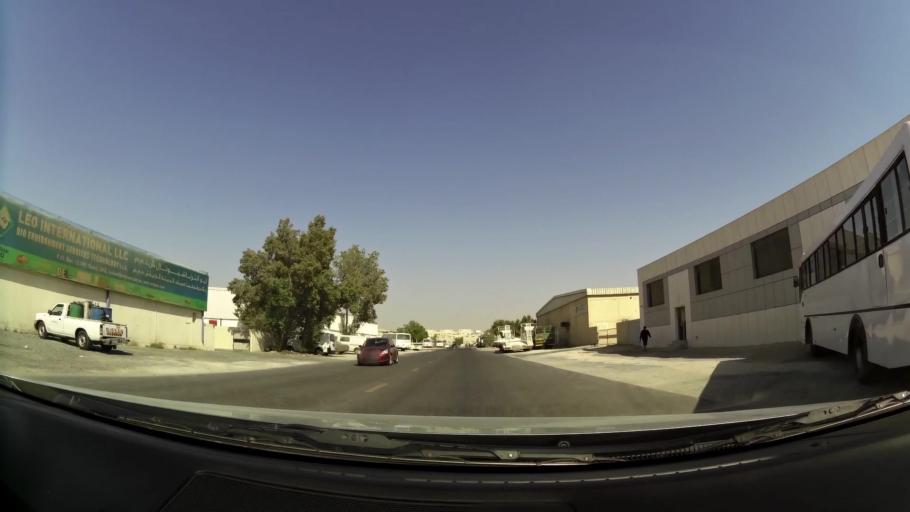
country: AE
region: Dubai
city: Dubai
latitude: 25.1256
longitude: 55.2242
